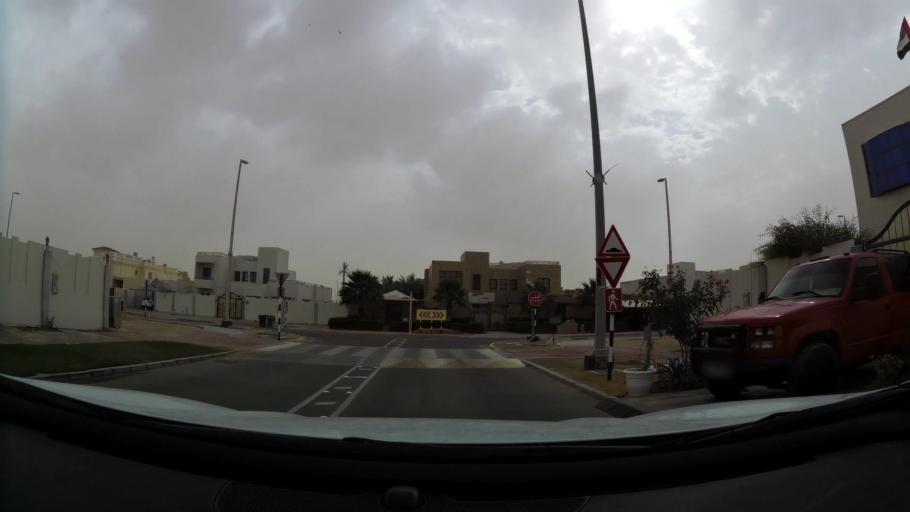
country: AE
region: Abu Dhabi
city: Abu Dhabi
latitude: 24.4532
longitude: 54.7214
